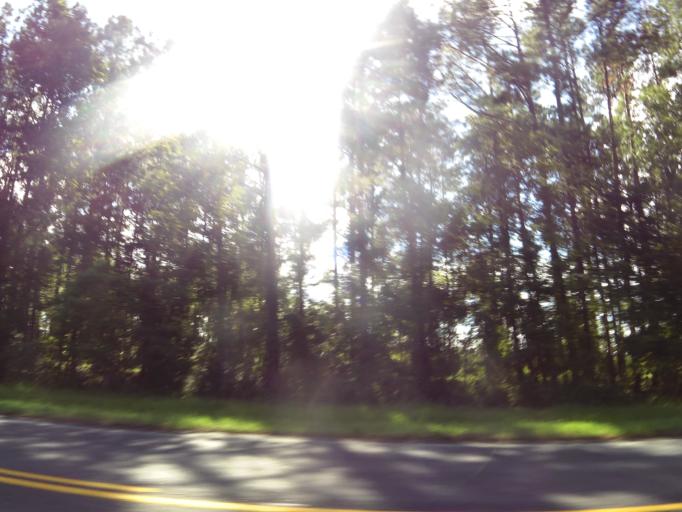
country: US
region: Georgia
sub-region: Camden County
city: Woodbine
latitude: 31.0209
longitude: -81.7311
